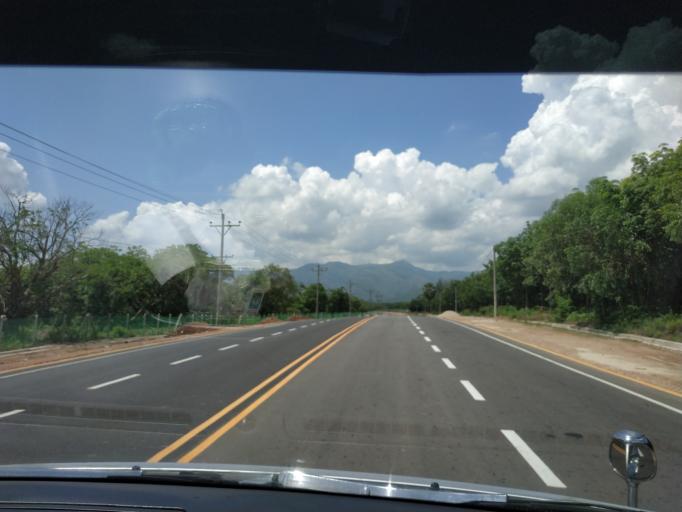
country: MM
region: Mon
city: Kyaikto
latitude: 17.3735
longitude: 97.0515
